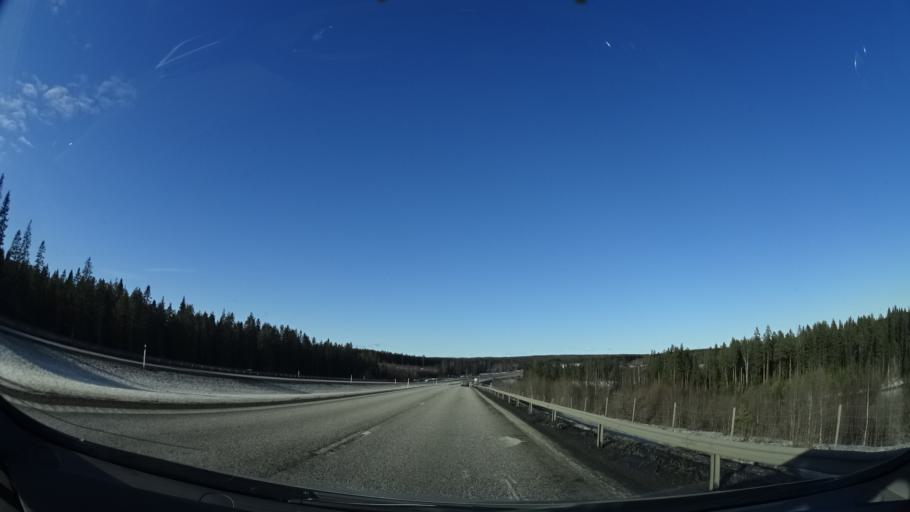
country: SE
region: Vaesterbotten
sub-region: Skelleftea Kommun
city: Kage
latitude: 64.7774
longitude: 21.0224
